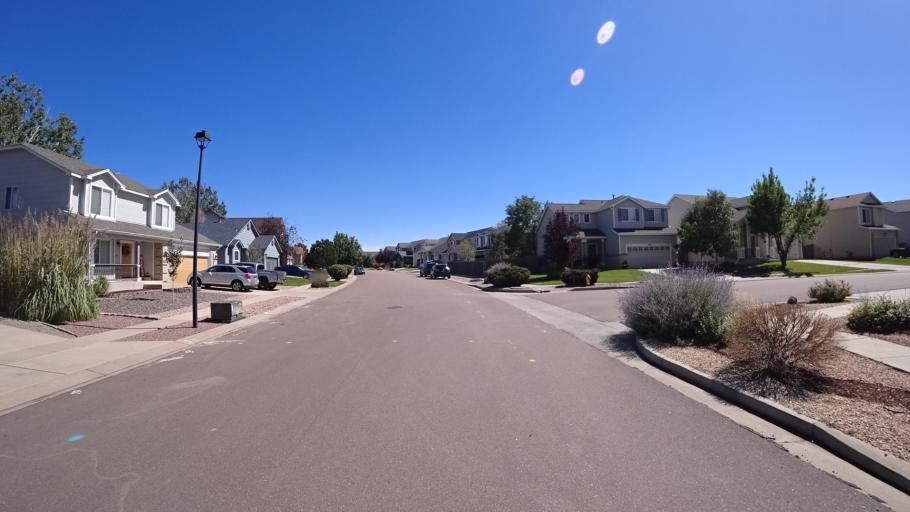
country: US
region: Colorado
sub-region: El Paso County
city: Security-Widefield
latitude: 38.7858
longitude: -104.7332
